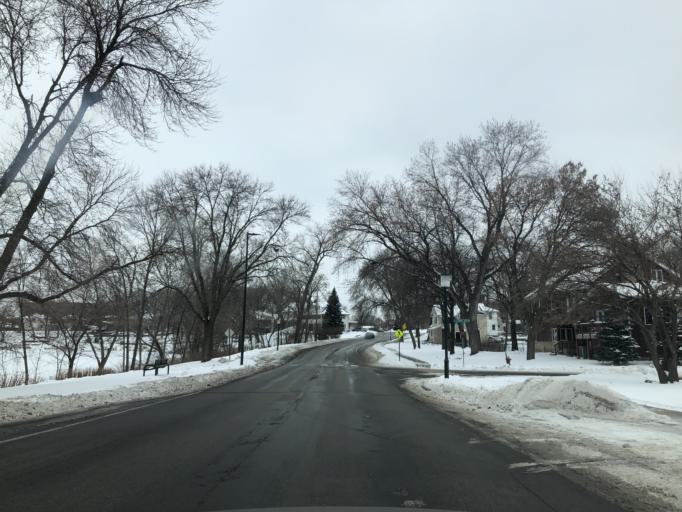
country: US
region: Minnesota
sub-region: Hennepin County
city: Robbinsdale
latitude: 45.0299
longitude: -93.3299
